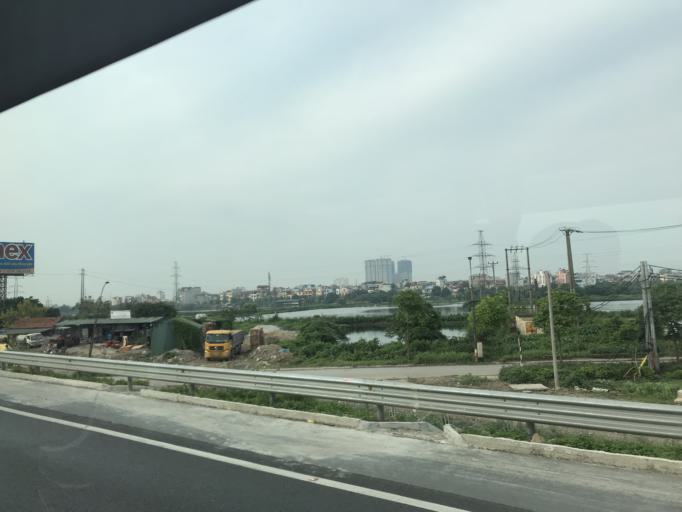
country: VN
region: Ha Noi
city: Van Dien
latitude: 20.9461
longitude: 105.8575
